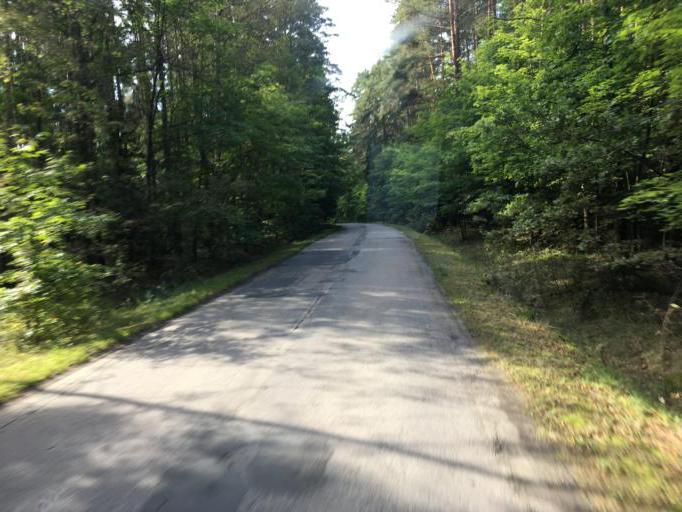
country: PL
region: Kujawsko-Pomorskie
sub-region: Powiat swiecki
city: Osie
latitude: 53.6067
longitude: 18.2590
